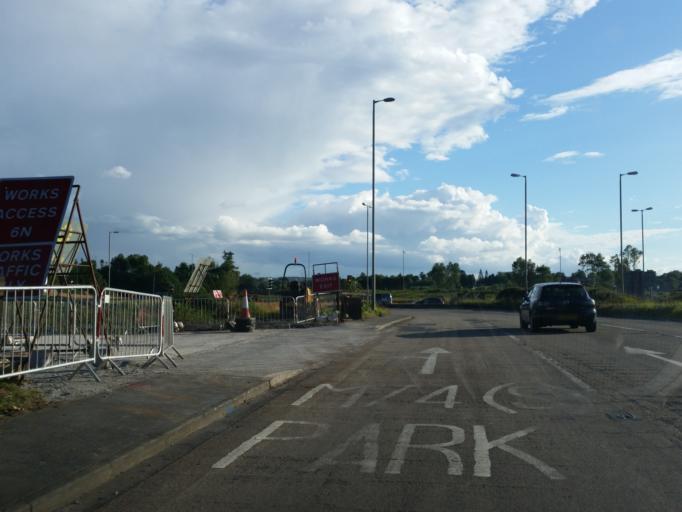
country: GB
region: Scotland
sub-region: South Lanarkshire
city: Bothwell
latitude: 55.8043
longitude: -4.0505
